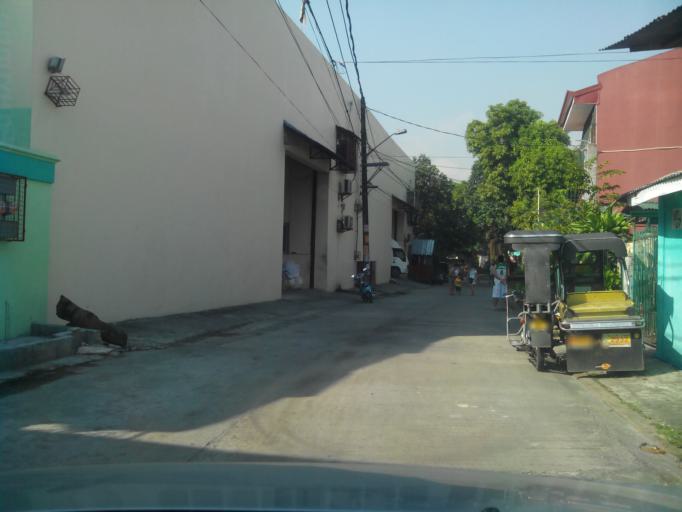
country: PH
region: Calabarzon
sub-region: Province of Rizal
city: Taytay
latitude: 14.5564
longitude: 121.1401
